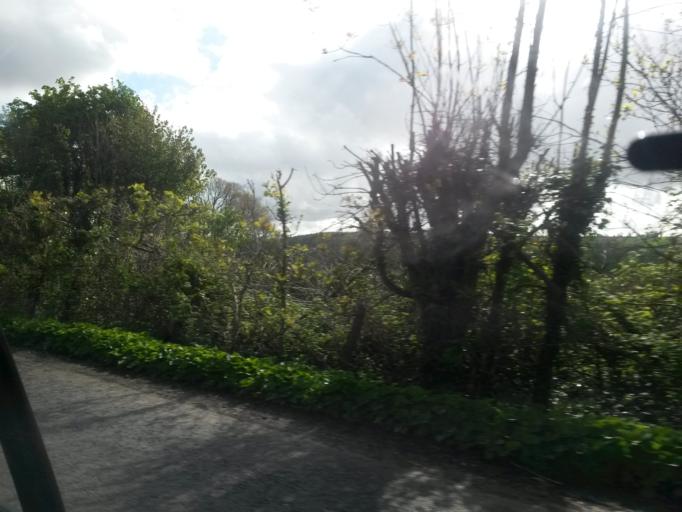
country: IE
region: Leinster
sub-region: Loch Garman
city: Ferns
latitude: 52.5659
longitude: -6.5258
